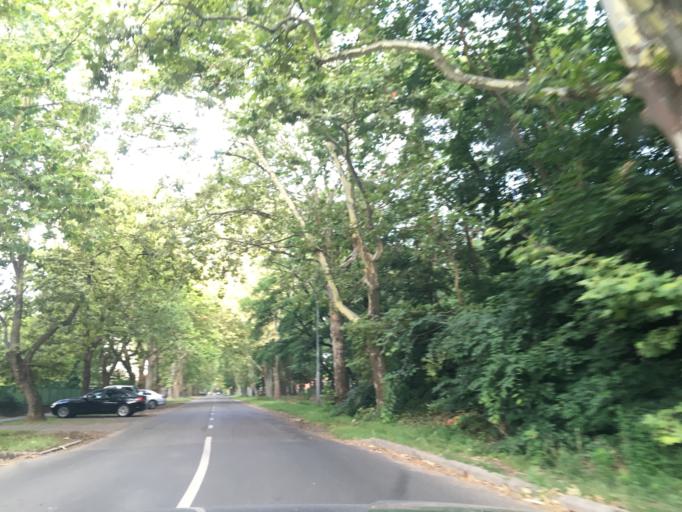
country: HU
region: Hajdu-Bihar
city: Debrecen
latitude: 47.5488
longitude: 21.6411
